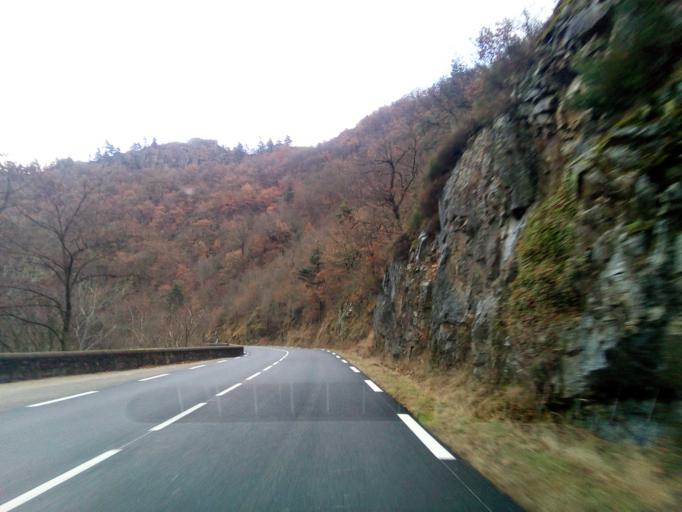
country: FR
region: Rhone-Alpes
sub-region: Departement de l'Ardeche
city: Saint-Sauveur-de-Montagut
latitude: 44.8808
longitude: 4.5216
